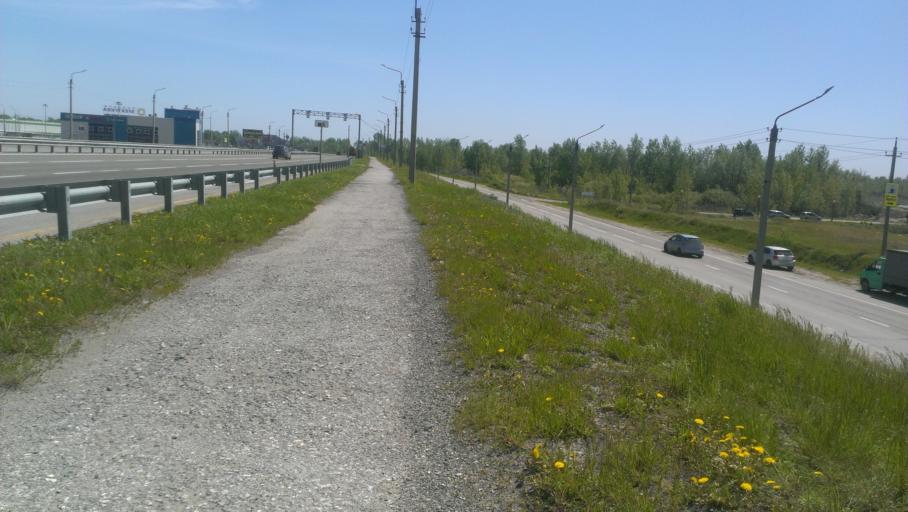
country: RU
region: Altai Krai
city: Zaton
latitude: 53.3174
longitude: 83.8208
